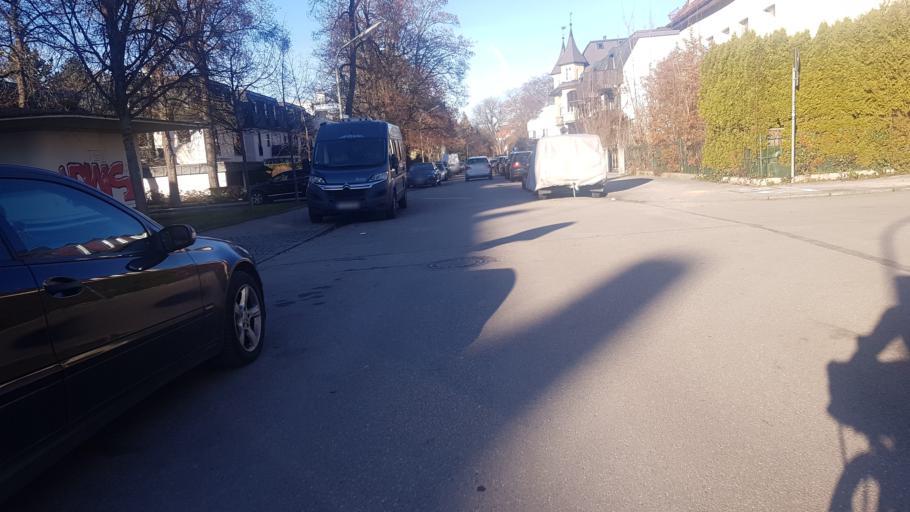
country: DE
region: Bavaria
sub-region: Upper Bavaria
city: Pasing
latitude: 48.1526
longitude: 11.5043
